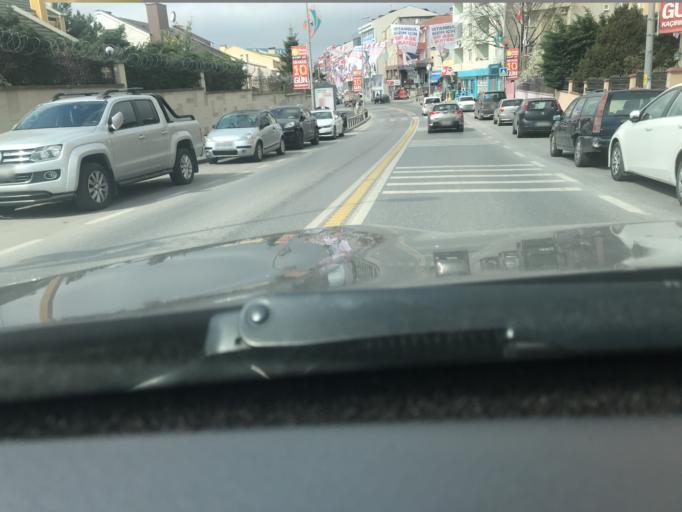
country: TR
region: Istanbul
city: Umraniye
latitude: 41.0323
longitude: 29.1787
